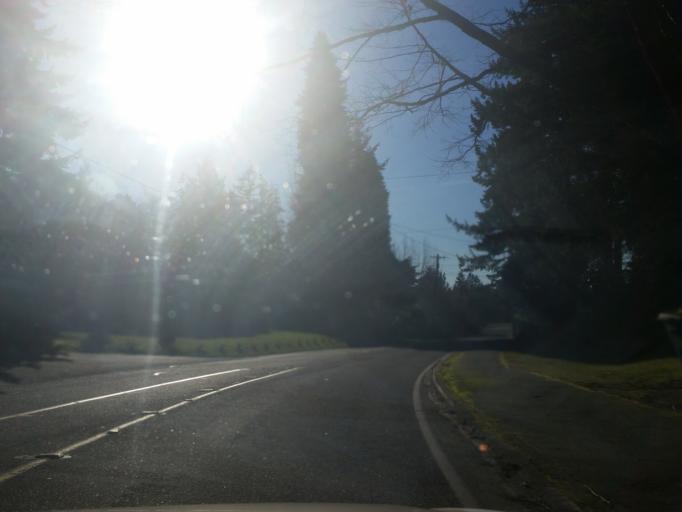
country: US
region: Washington
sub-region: Snohomish County
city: Edmonds
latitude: 47.8236
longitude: -122.3619
